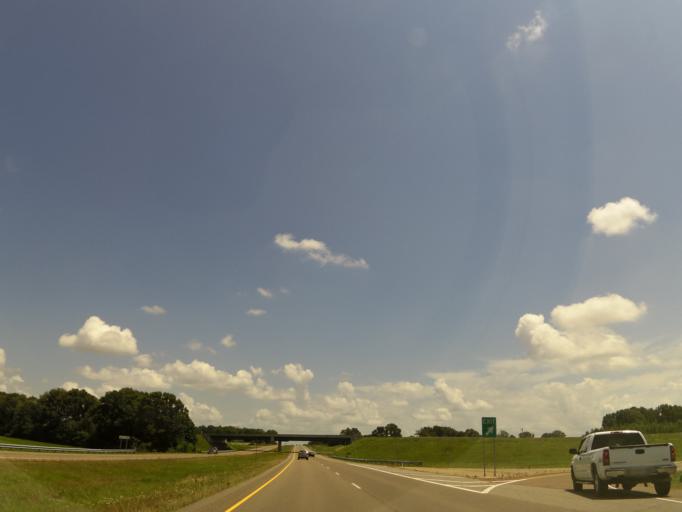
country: US
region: Tennessee
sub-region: Crockett County
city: Alamo
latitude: 35.8378
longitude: -89.1871
